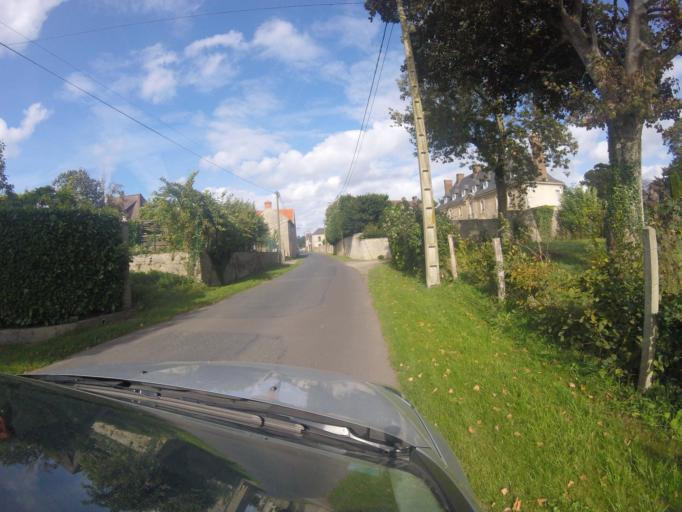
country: FR
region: Lower Normandy
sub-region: Departement du Calvados
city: Saint-Vigor-le-Grand
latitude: 49.3391
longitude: -0.6925
